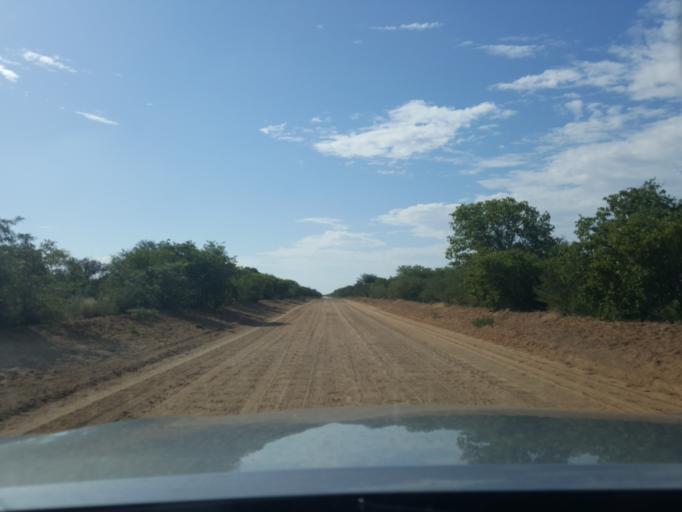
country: BW
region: Kweneng
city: Khudumelapye
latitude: -23.5048
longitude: 24.7087
